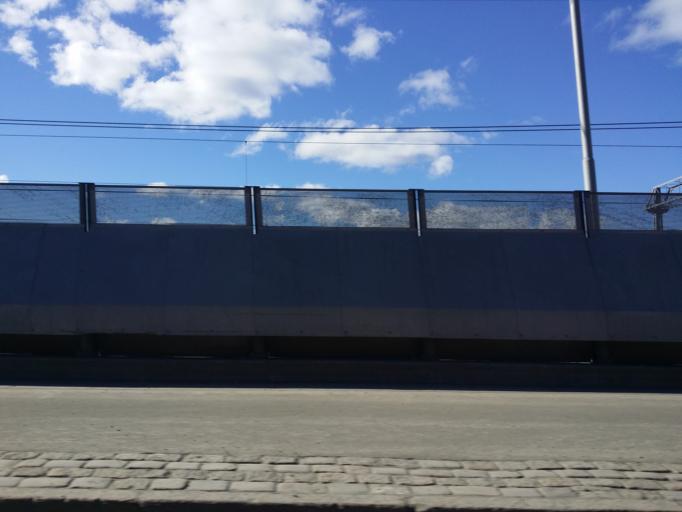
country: NO
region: Oslo
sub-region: Oslo
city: Oslo
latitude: 59.8991
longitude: 10.7564
